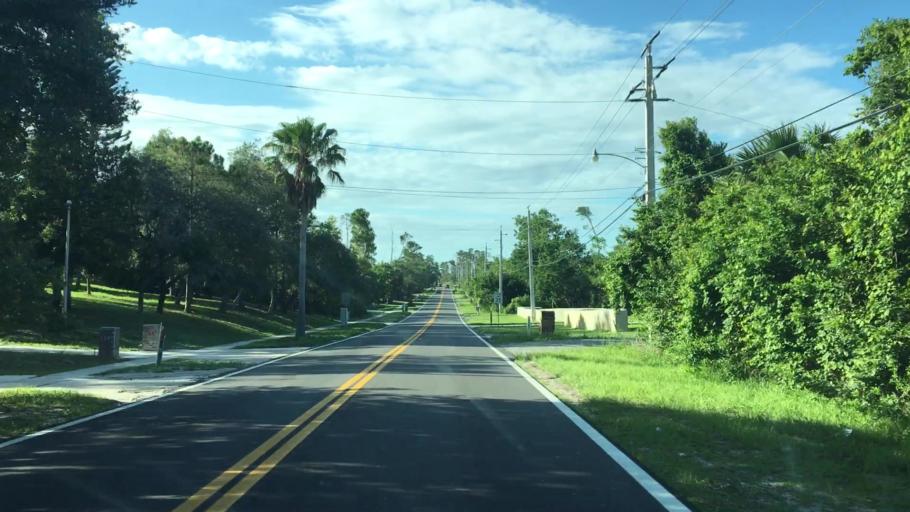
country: US
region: Florida
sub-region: Brevard County
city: Mims
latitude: 28.6327
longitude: -80.8605
